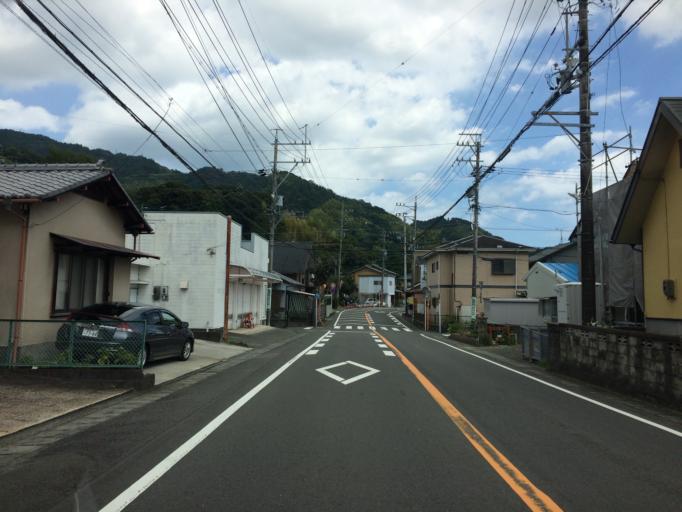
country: JP
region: Shizuoka
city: Yaizu
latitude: 34.9040
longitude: 138.2932
